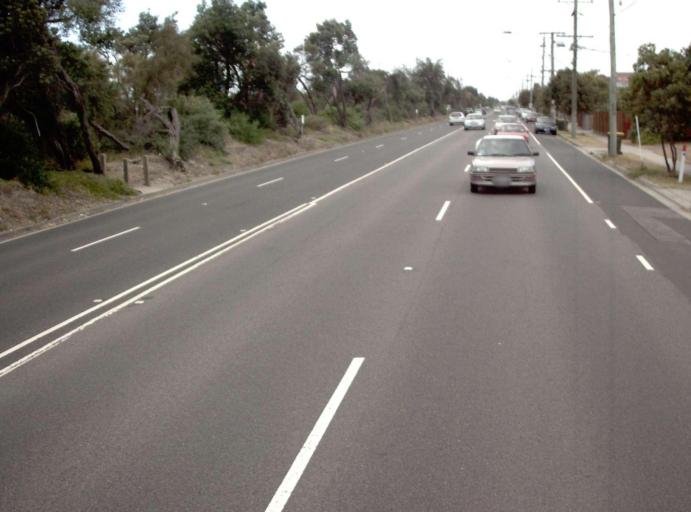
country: AU
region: Victoria
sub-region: Frankston
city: Seaford
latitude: -38.1013
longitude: 145.1259
